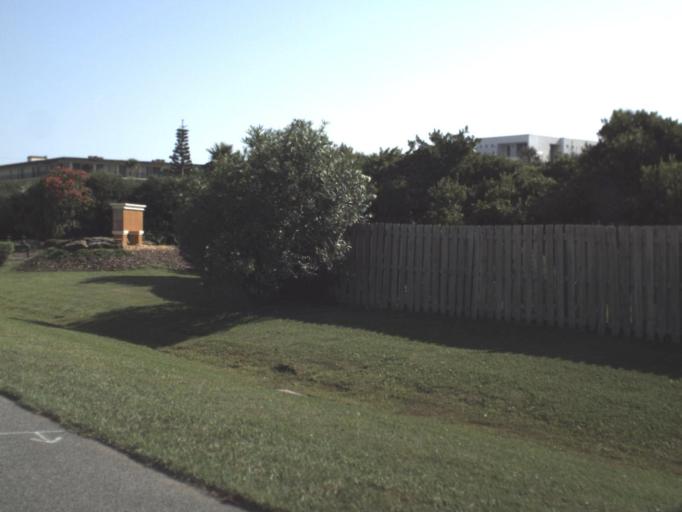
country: US
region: Florida
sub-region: Saint Johns County
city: Butler Beach
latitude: 29.7387
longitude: -81.2425
